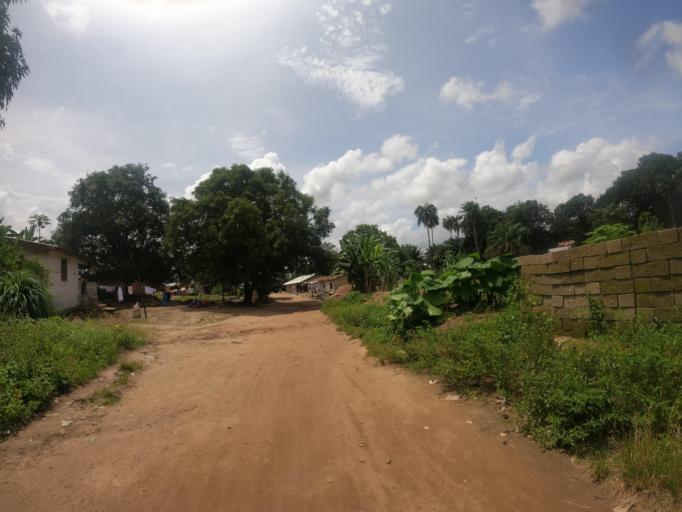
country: SL
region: Northern Province
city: Makeni
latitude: 8.9005
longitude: -12.0564
